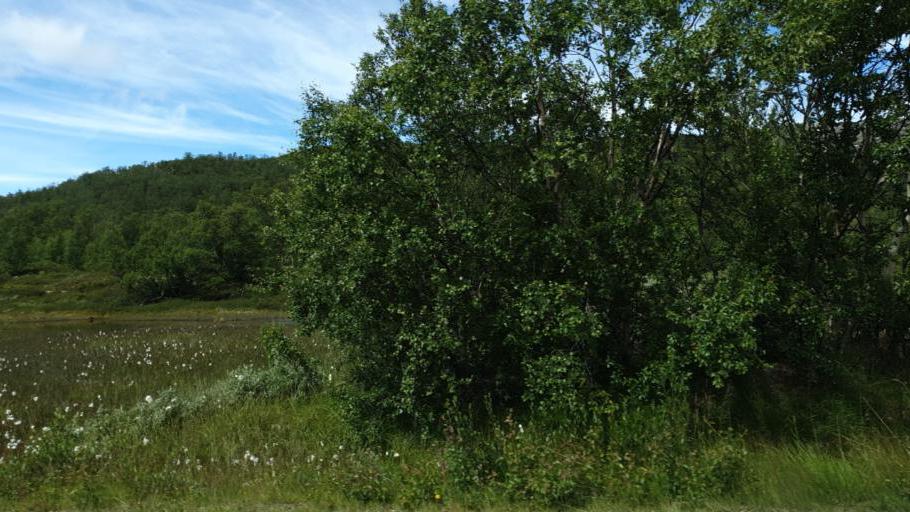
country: NO
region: Oppland
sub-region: Oystre Slidre
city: Heggenes
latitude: 61.4928
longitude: 8.8428
